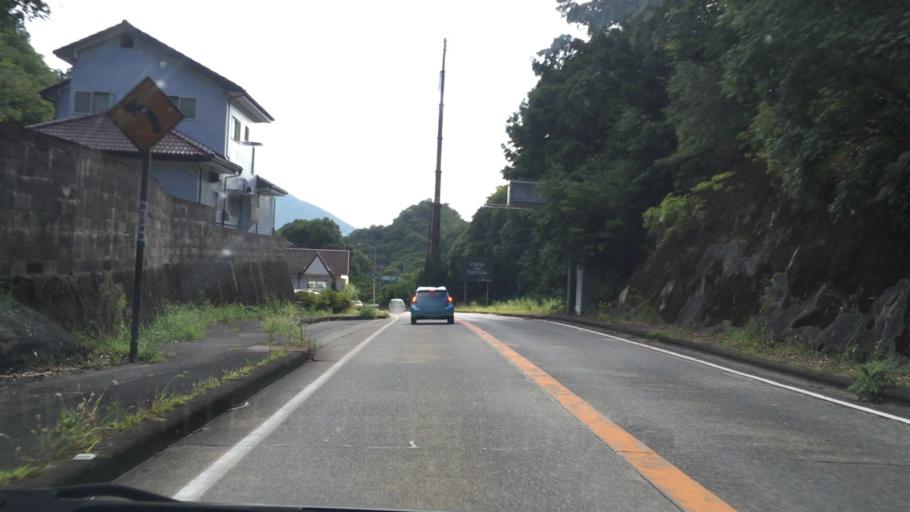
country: JP
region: Saga Prefecture
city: Imaricho-ko
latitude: 33.1868
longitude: 129.8971
